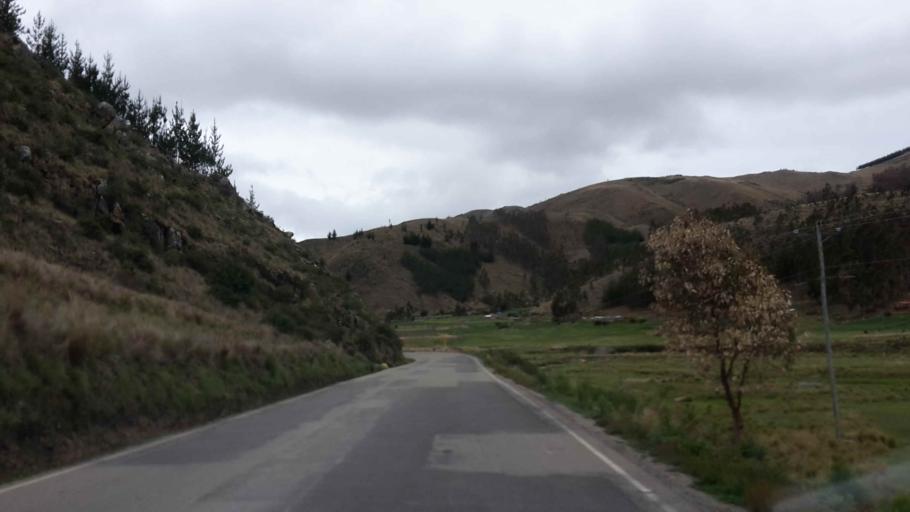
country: BO
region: Cochabamba
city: Arani
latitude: -17.4851
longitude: -65.5514
